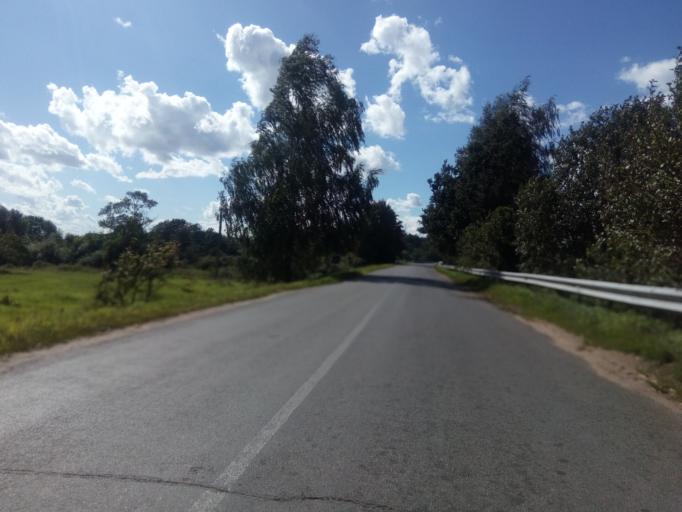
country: BY
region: Vitebsk
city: Dzisna
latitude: 55.7017
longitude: 28.1915
